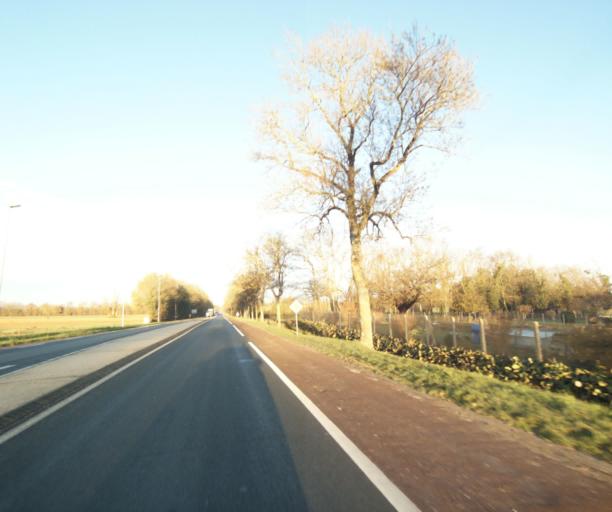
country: FR
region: Poitou-Charentes
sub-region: Departement de la Charente-Maritime
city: Saint-Georges-des-Coteaux
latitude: 45.7785
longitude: -0.7020
